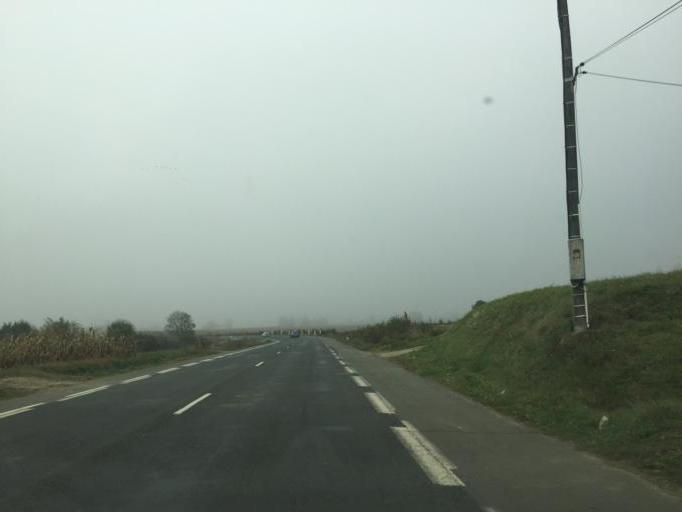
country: FR
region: Rhone-Alpes
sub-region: Departement de l'Ain
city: Miribel
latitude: 45.8289
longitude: 4.9382
